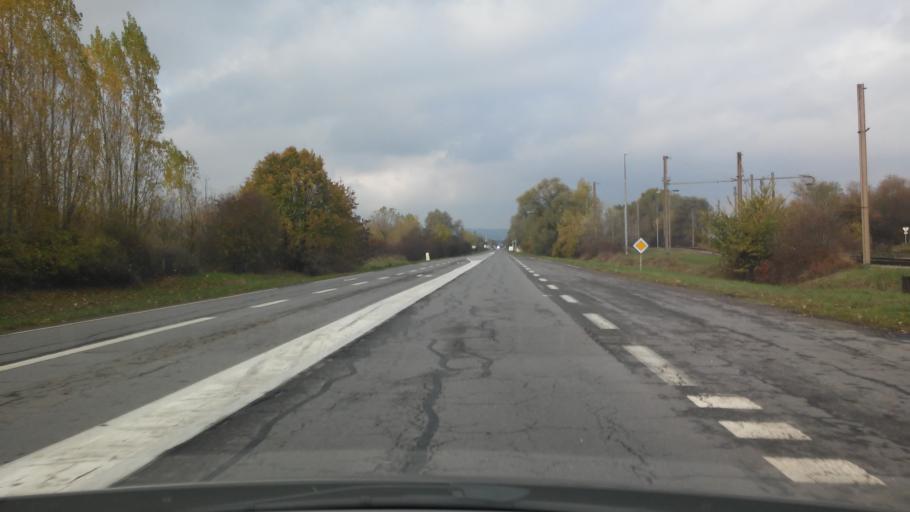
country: FR
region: Lorraine
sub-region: Departement de la Moselle
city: Uckange
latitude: 49.3129
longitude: 6.1580
